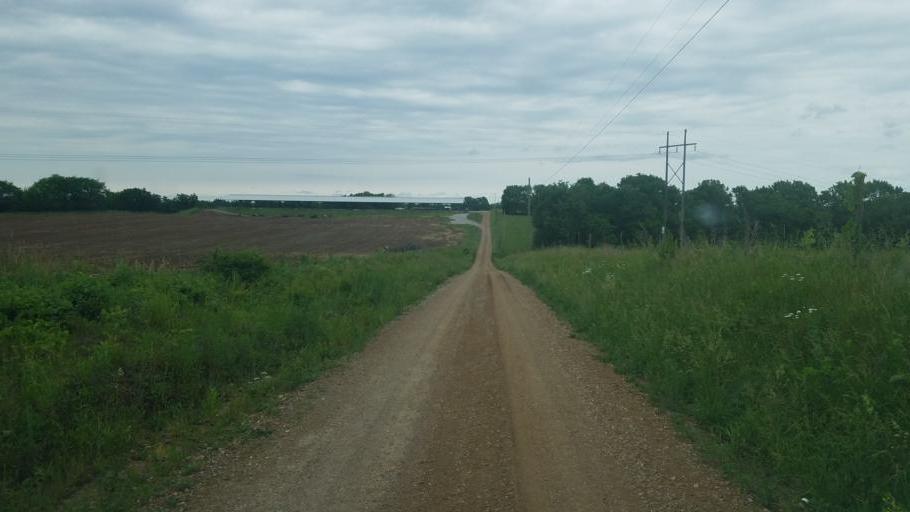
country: US
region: Missouri
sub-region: Moniteau County
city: California
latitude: 38.5975
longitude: -92.6476
